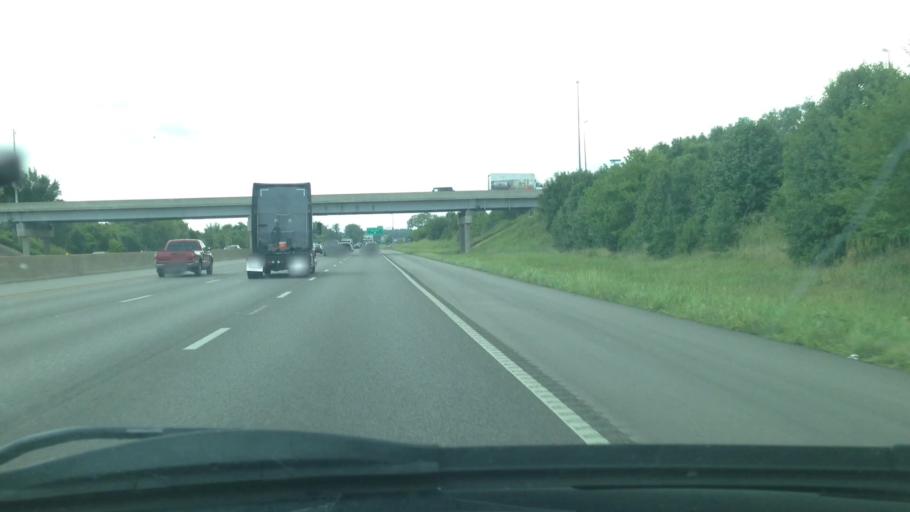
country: US
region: Missouri
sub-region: Saint Charles County
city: Weldon Spring
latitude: 38.6749
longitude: -90.6440
